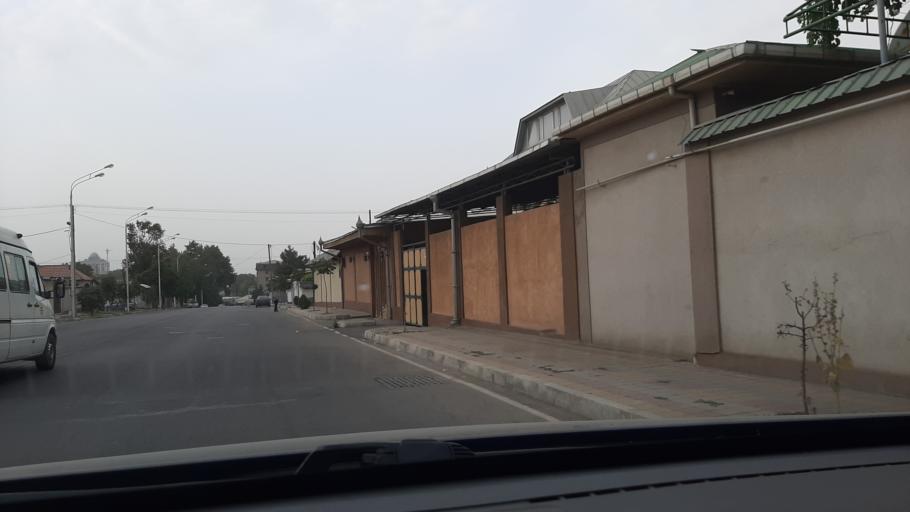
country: TJ
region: Dushanbe
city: Dushanbe
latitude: 38.6108
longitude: 68.7826
